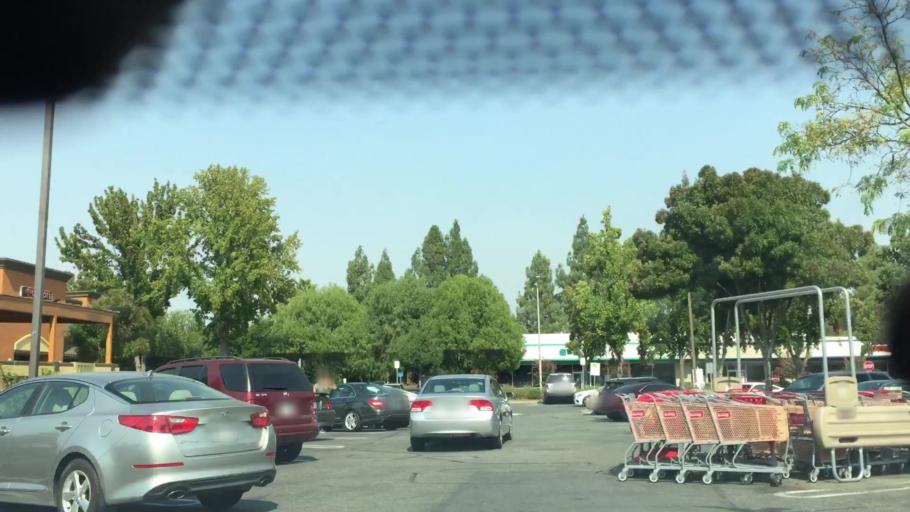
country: US
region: California
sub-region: Contra Costa County
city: Pacheco
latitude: 37.9784
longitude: -122.0672
